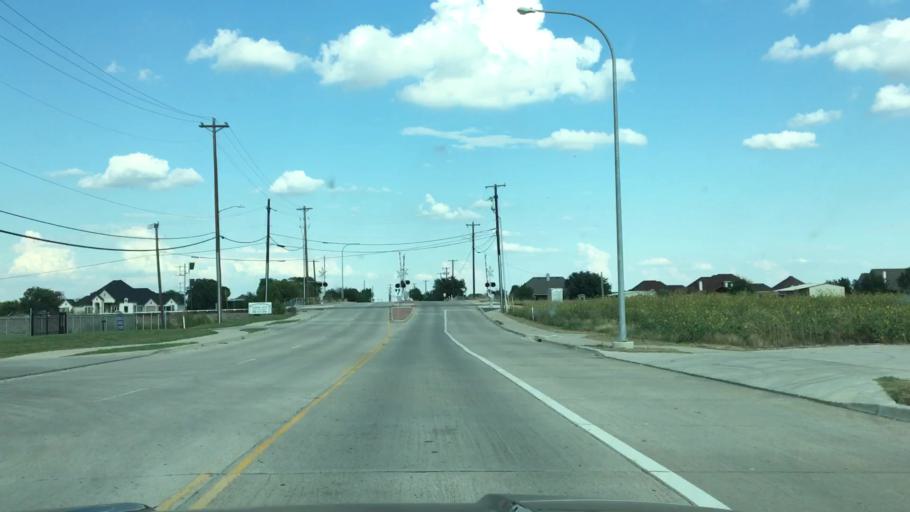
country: US
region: Texas
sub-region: Tarrant County
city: Haslet
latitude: 32.9688
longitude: -97.4053
